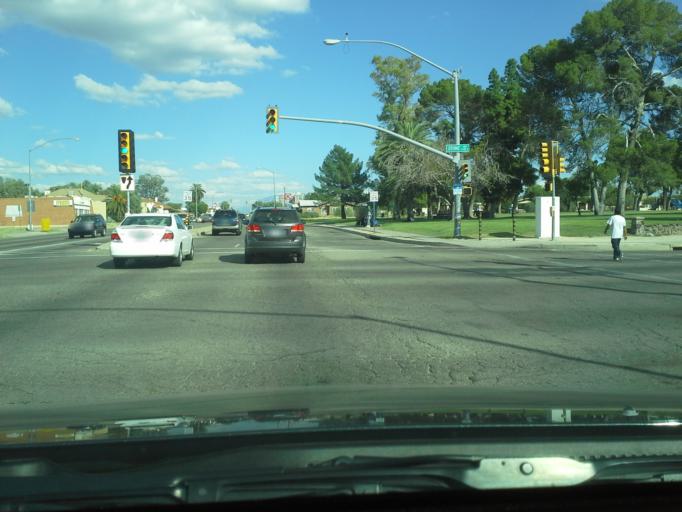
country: US
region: Arizona
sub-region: Pima County
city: South Tucson
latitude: 32.2359
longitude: -110.9721
